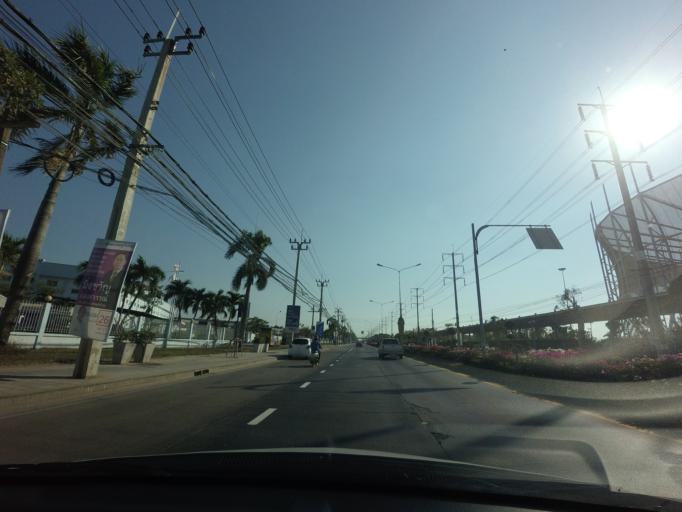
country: TH
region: Bangkok
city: Nong Chok
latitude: 13.8323
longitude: 100.8509
